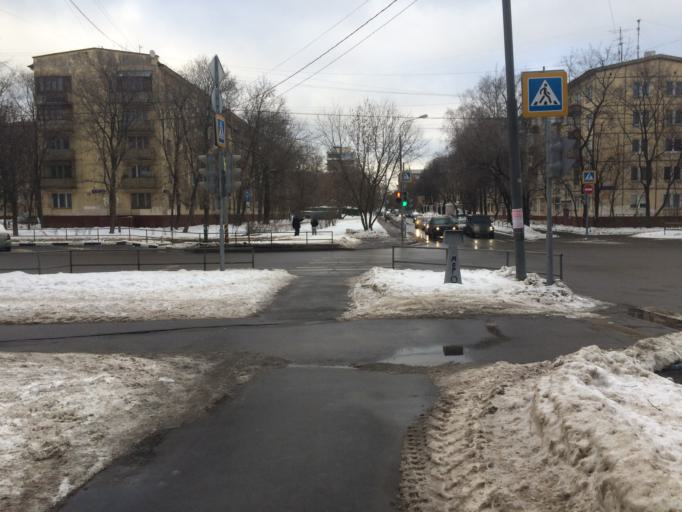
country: RU
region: Moscow
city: Sokol
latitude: 55.8005
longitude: 37.5487
